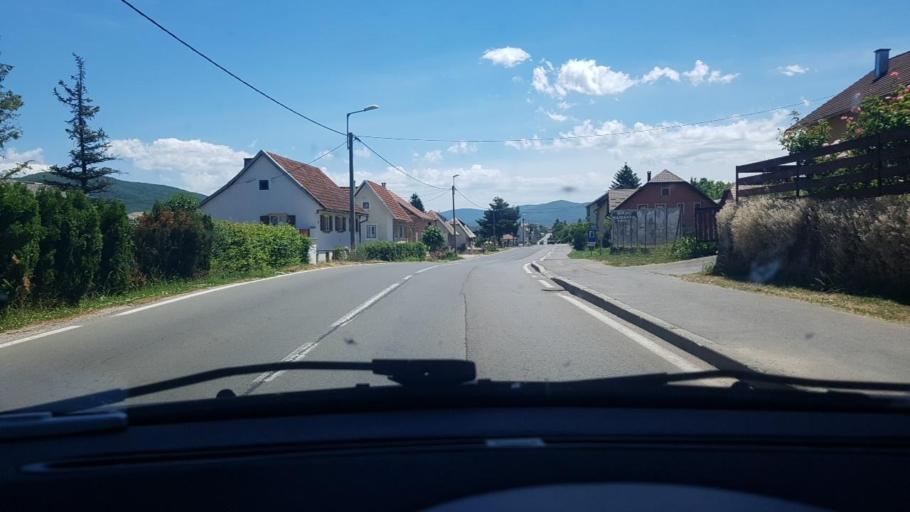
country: HR
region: Licko-Senjska
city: Otocac
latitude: 44.8684
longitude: 15.2473
